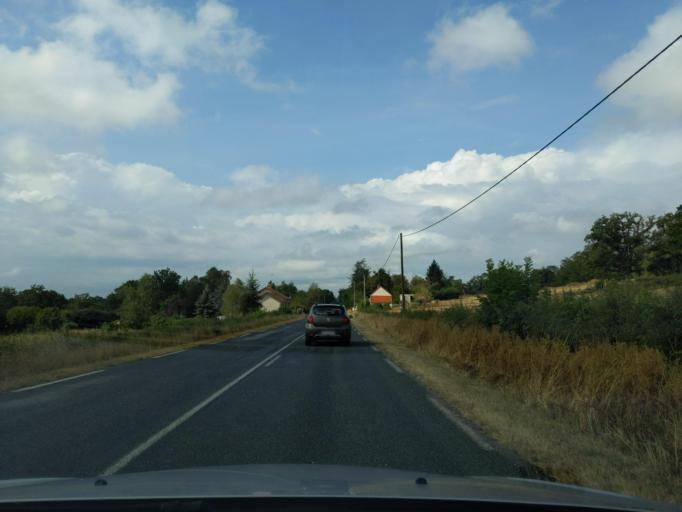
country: FR
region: Bourgogne
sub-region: Departement de Saone-et-Loire
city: Bourbon-Lancy
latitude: 46.6768
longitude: 3.8120
